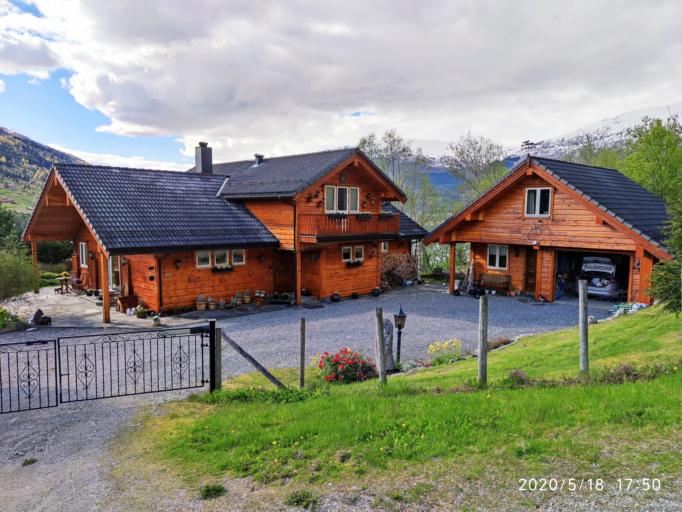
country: NO
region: Sogn og Fjordane
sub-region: Stryn
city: Stryn
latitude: 61.8422
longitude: 6.8171
